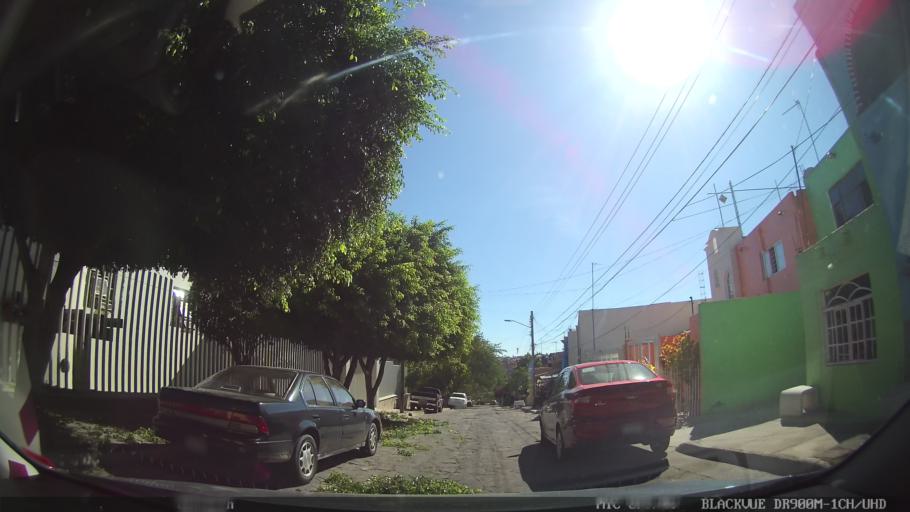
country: MX
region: Jalisco
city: Tlaquepaque
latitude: 20.6817
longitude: -103.2693
